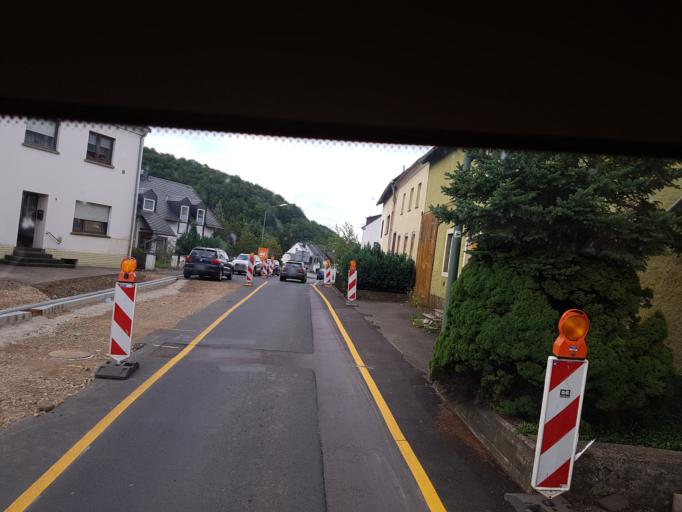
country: DE
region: Rheinland-Pfalz
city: Pelm
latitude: 50.2341
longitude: 6.6909
